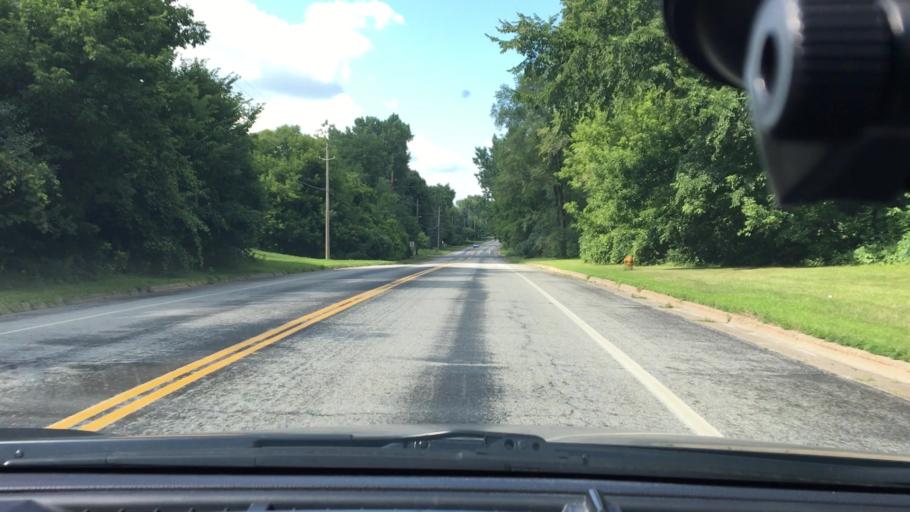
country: US
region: Minnesota
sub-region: Hennepin County
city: Plymouth
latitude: 45.0353
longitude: -93.4360
